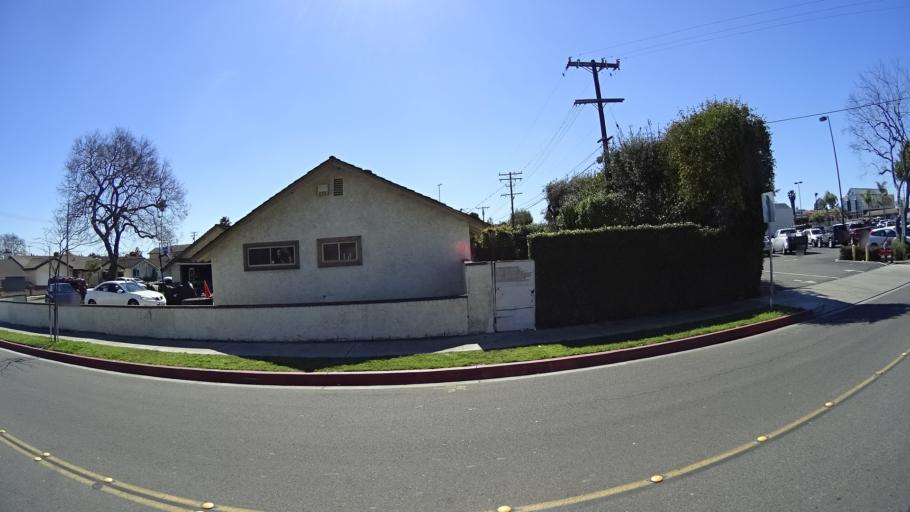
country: US
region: California
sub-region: Orange County
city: Stanton
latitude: 33.8251
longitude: -117.9575
